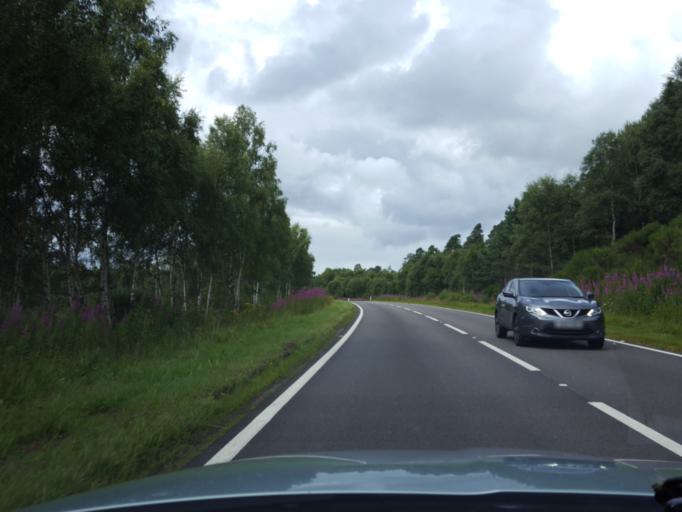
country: GB
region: Scotland
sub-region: Highland
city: Grantown on Spey
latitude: 57.2816
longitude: -3.6799
